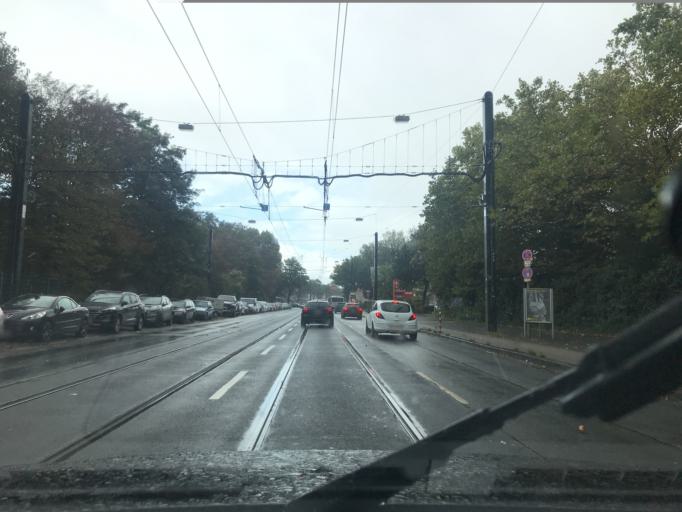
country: DE
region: North Rhine-Westphalia
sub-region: Regierungsbezirk Dusseldorf
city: Dusseldorf
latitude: 51.2609
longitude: 6.7770
